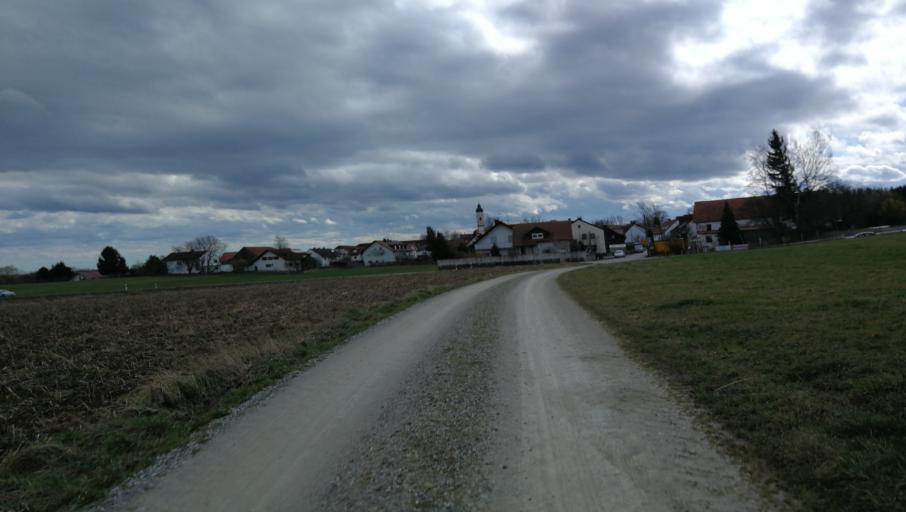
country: DE
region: Bavaria
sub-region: Upper Bavaria
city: Fuerstenfeldbruck
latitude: 48.1928
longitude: 11.2201
